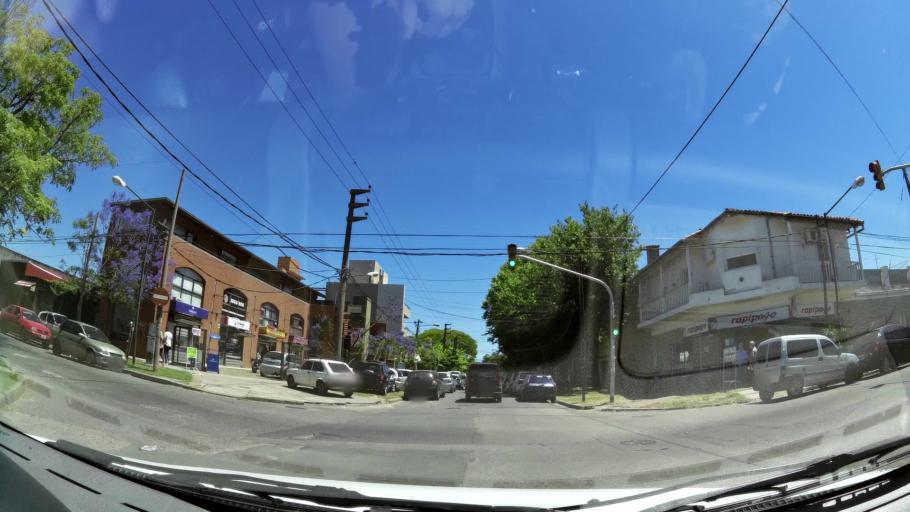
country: AR
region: Buenos Aires
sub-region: Partido de San Isidro
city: San Isidro
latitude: -34.5079
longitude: -58.5635
